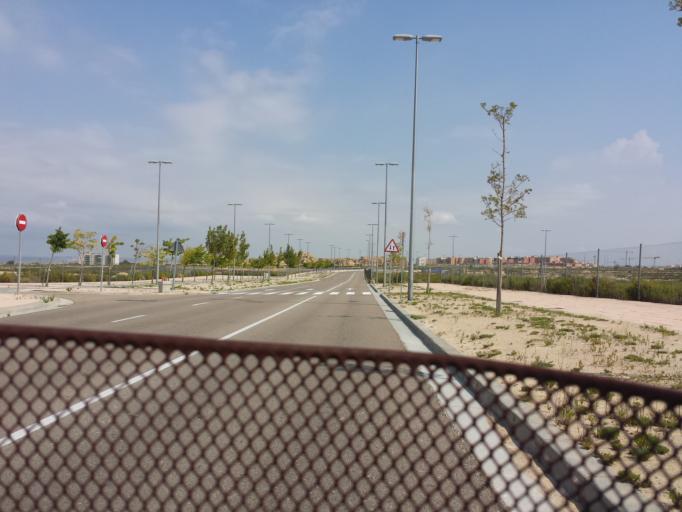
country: ES
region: Aragon
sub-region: Provincia de Zaragoza
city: Montecanal
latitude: 41.6272
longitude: -0.9564
